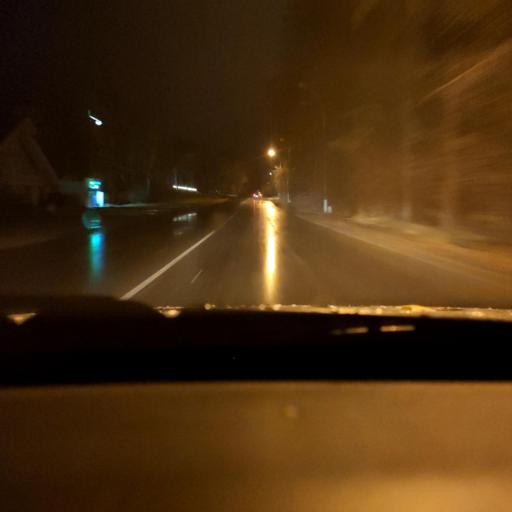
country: RU
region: Perm
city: Kultayevo
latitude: 58.0108
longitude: 55.9807
